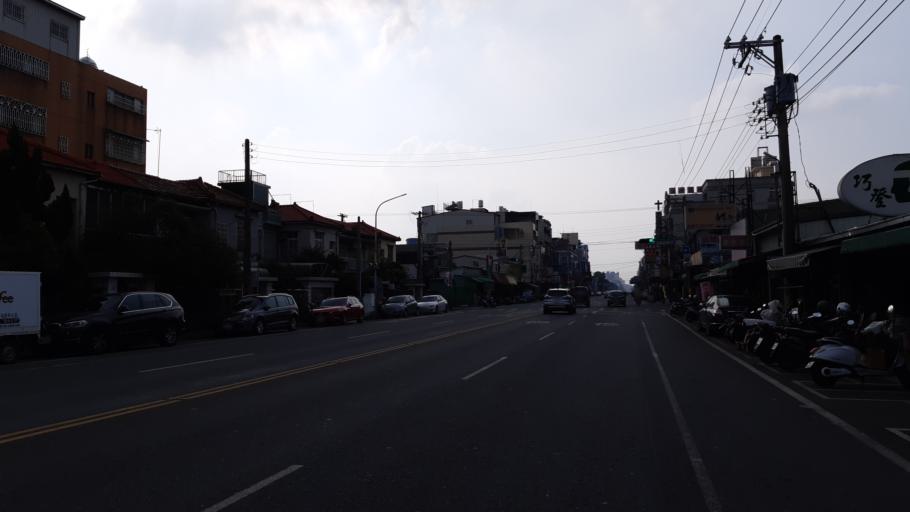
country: TW
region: Taiwan
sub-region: Chiayi
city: Jiayi Shi
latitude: 23.4698
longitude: 120.4580
